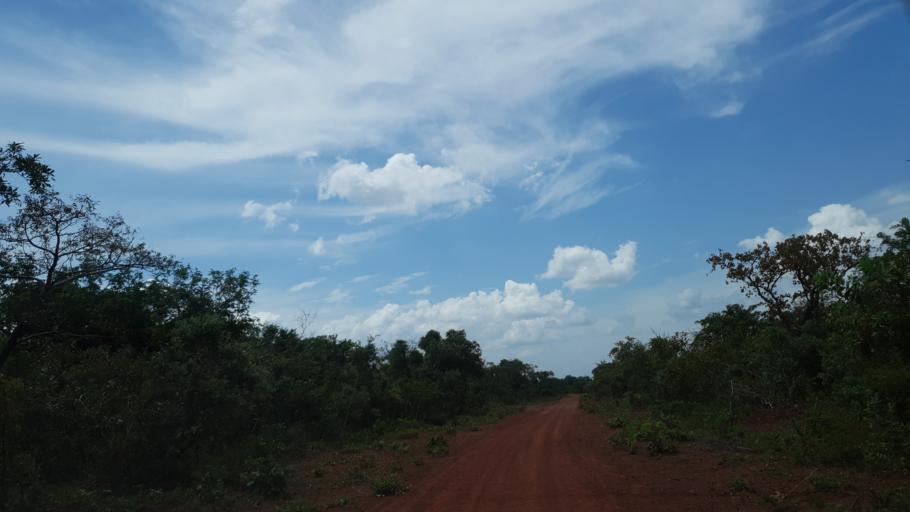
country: ML
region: Sikasso
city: Sikasso
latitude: 11.6862
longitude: -6.2145
